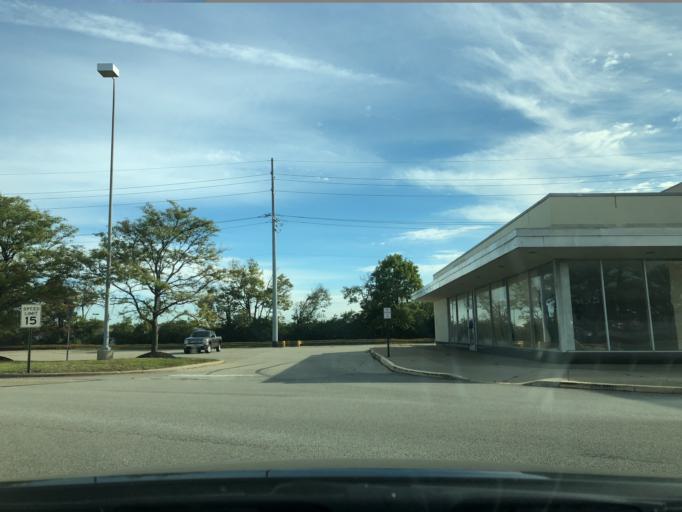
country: US
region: Ohio
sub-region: Hamilton County
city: Glendale
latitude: 39.2882
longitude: -84.4614
